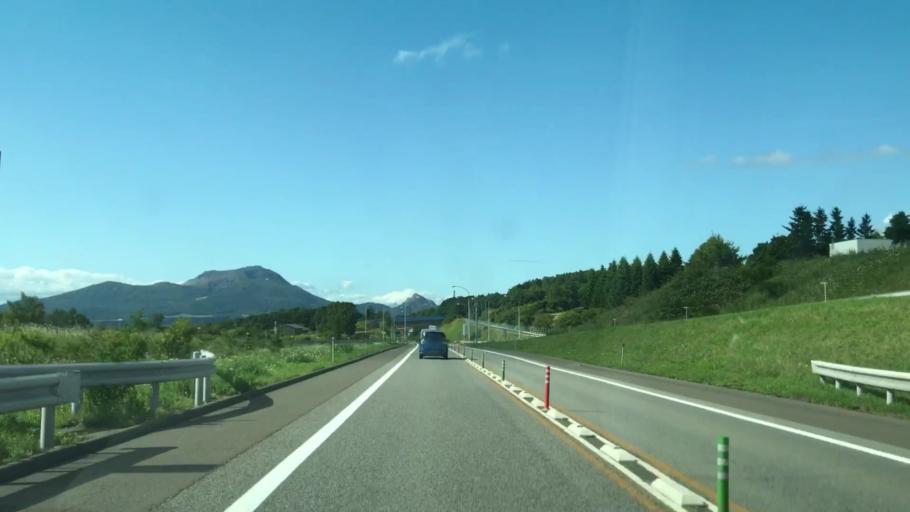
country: JP
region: Hokkaido
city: Date
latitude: 42.4663
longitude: 140.9087
